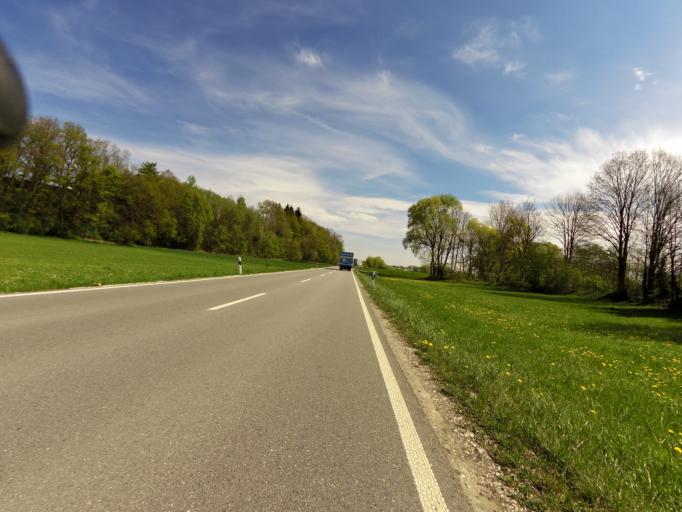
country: DE
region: Bavaria
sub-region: Upper Bavaria
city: Wang
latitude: 48.5102
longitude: 11.9736
